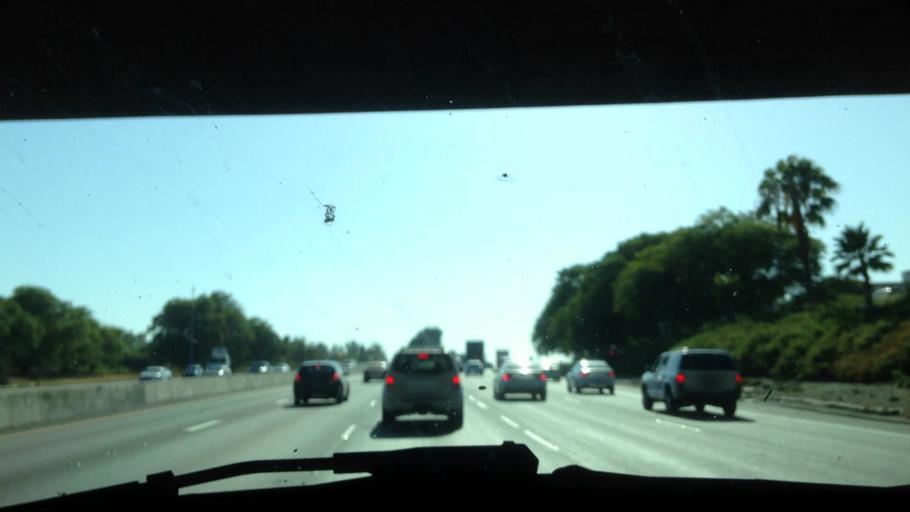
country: US
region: California
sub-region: Orange County
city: Anaheim
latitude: 33.8396
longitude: -117.9127
